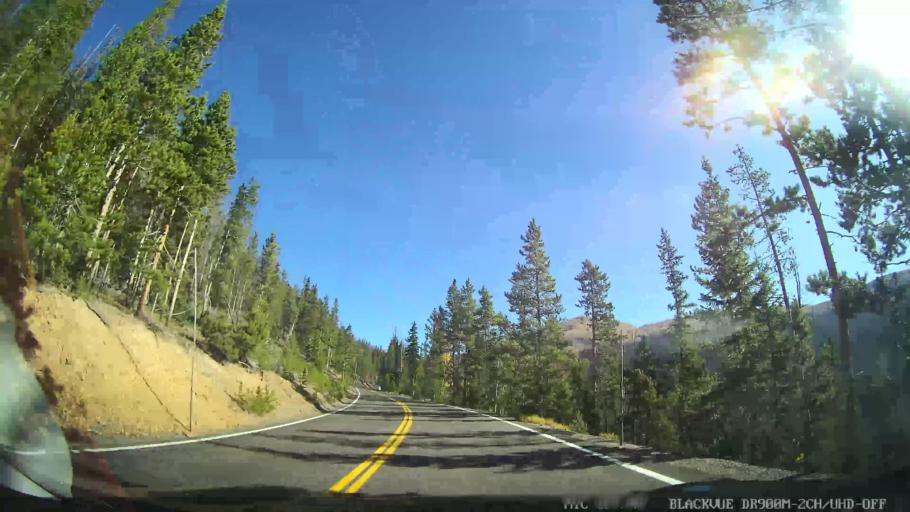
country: US
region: Colorado
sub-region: Larimer County
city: Estes Park
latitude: 40.4042
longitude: -105.8246
